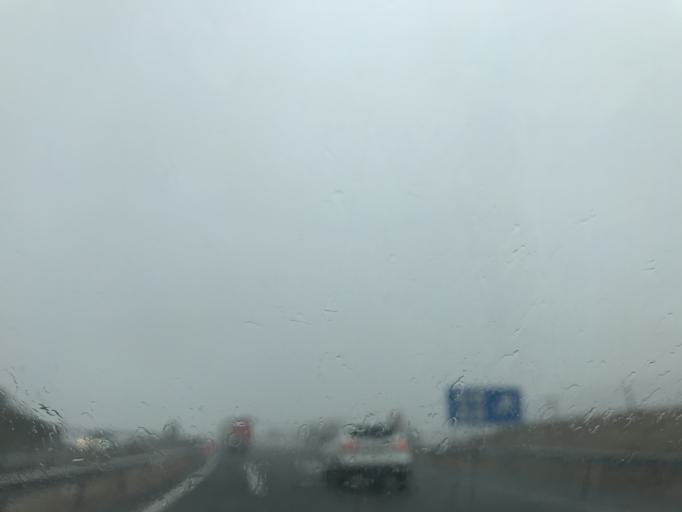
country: ES
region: Andalusia
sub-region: Provincia de Malaga
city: Villanueva del Rosario
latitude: 36.9837
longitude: -4.4604
